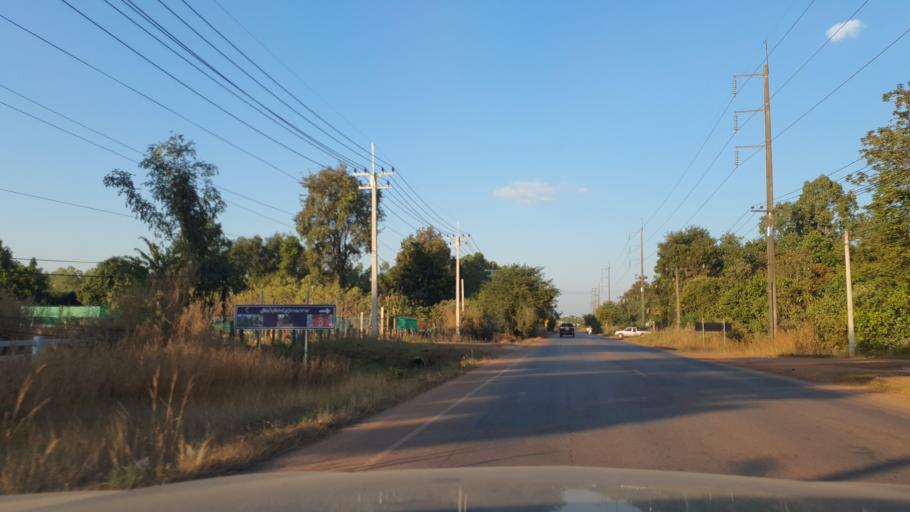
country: TH
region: Nakhon Phanom
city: Si Songkhram
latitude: 17.6027
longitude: 104.2396
